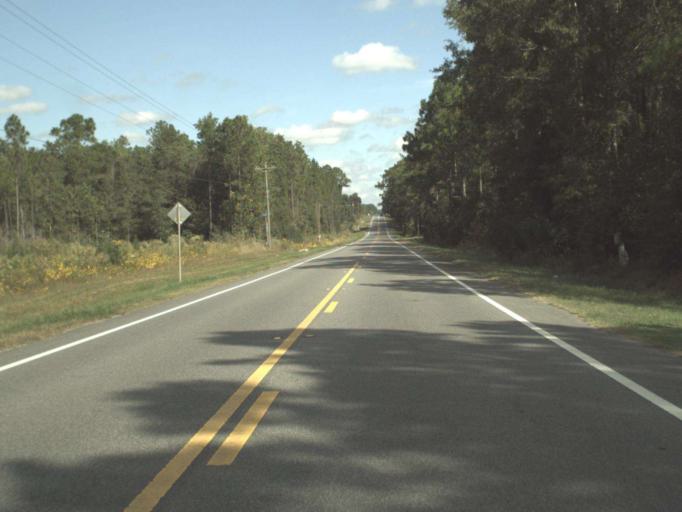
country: US
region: Florida
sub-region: Walton County
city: DeFuniak Springs
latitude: 30.8157
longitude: -86.1231
